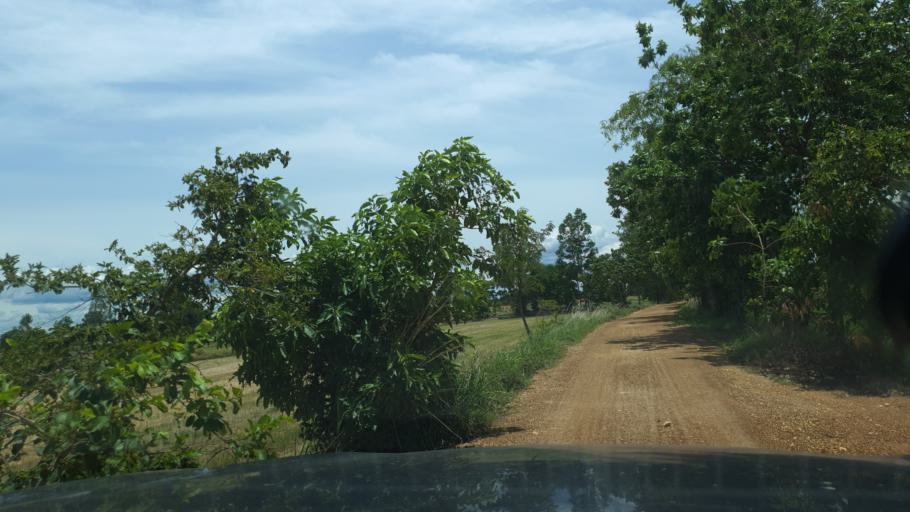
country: TH
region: Sukhothai
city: Ban Na
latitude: 17.1330
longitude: 99.6700
